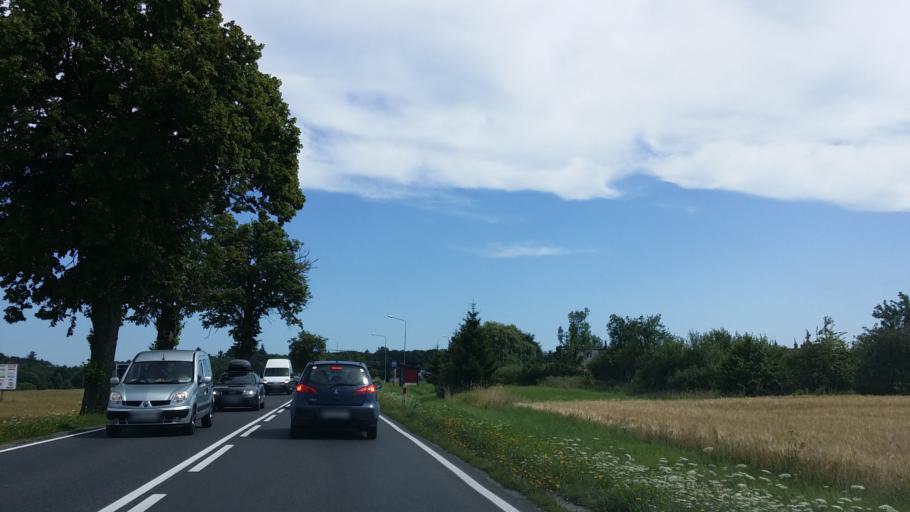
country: PL
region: West Pomeranian Voivodeship
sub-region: Powiat kolobrzeski
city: Kolobrzeg
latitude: 54.1805
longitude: 15.6317
